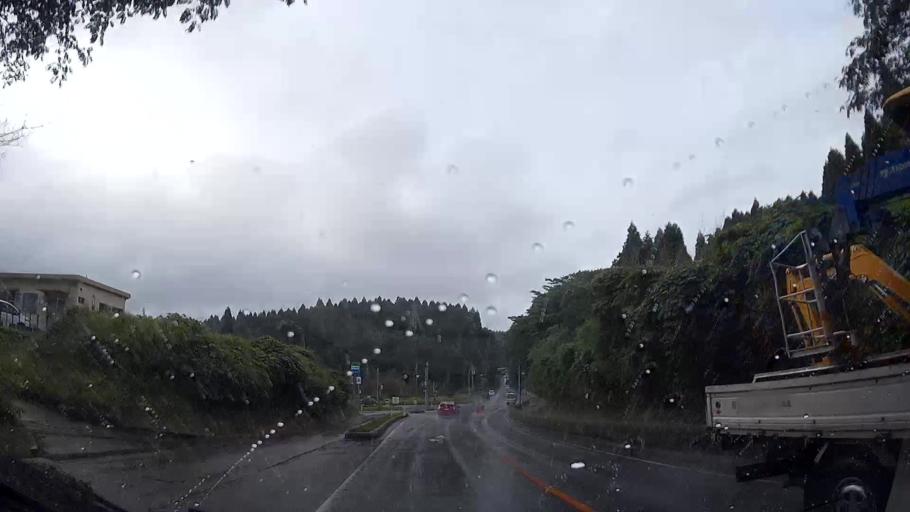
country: JP
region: Kumamoto
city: Aso
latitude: 32.8641
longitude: 131.0007
